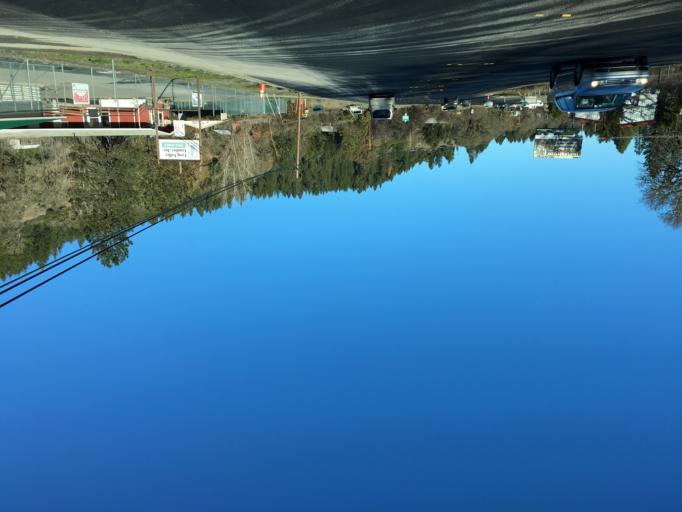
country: US
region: California
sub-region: Mendocino County
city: Laytonville
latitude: 39.6799
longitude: -123.4760
